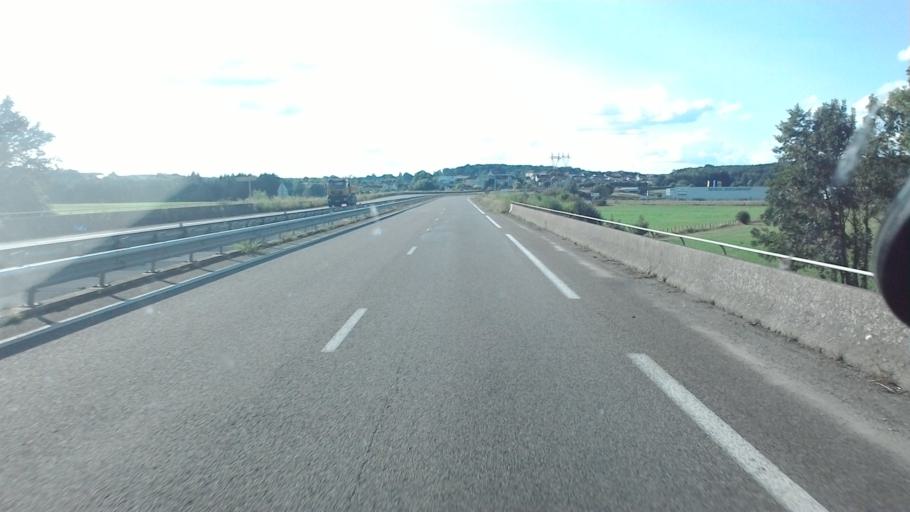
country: FR
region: Franche-Comte
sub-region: Departement de la Haute-Saone
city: Saint-Sauveur
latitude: 47.8127
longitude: 6.3993
